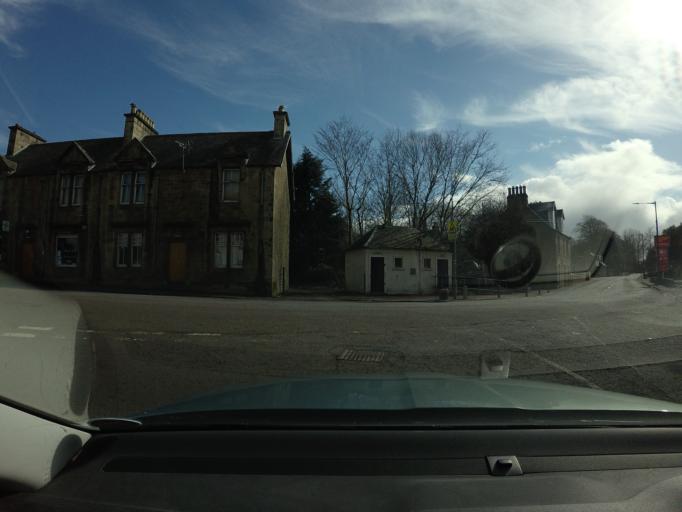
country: GB
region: Scotland
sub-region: South Lanarkshire
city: Douglas
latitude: 55.5557
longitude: -3.8482
